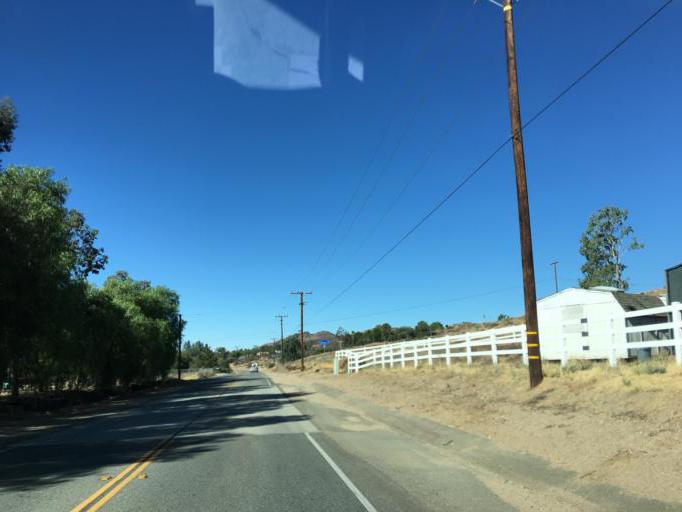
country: US
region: California
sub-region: Los Angeles County
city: Agua Dulce
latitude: 34.5064
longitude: -118.3212
